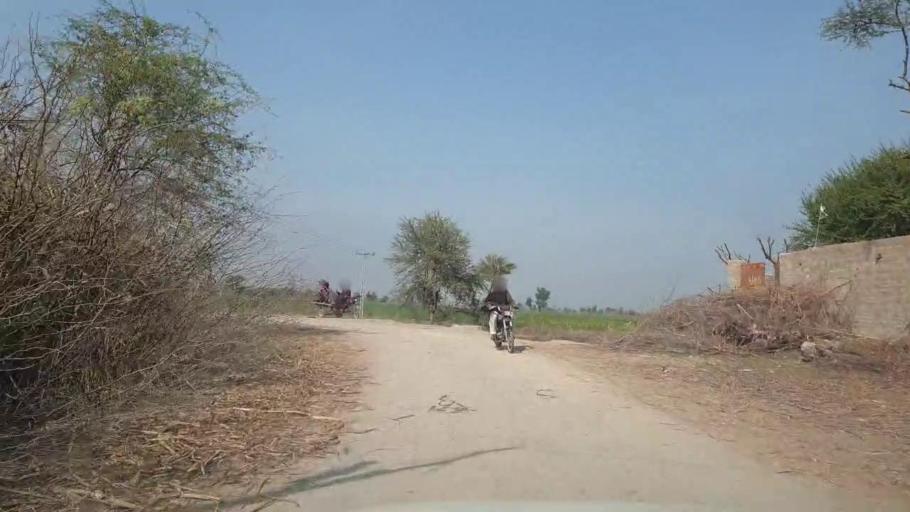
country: PK
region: Sindh
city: Mirpur Khas
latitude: 25.6873
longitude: 69.1552
